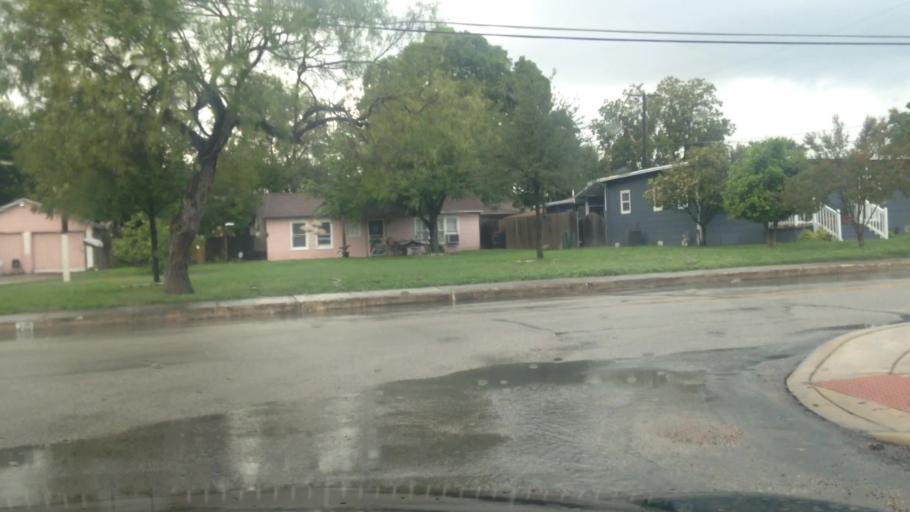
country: US
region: Texas
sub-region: Bexar County
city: Balcones Heights
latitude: 29.4829
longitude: -98.5478
